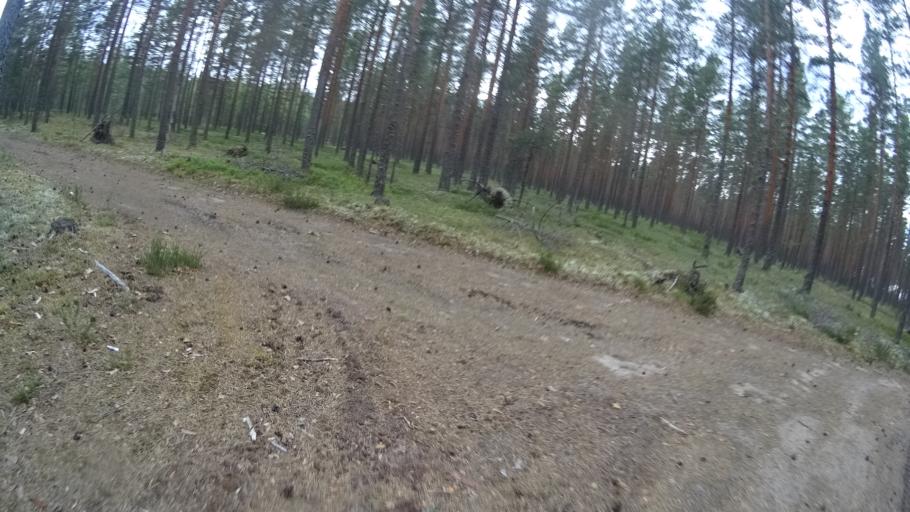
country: FI
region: Satakunta
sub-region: Pohjois-Satakunta
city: Jaemijaervi
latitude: 61.7698
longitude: 22.7655
